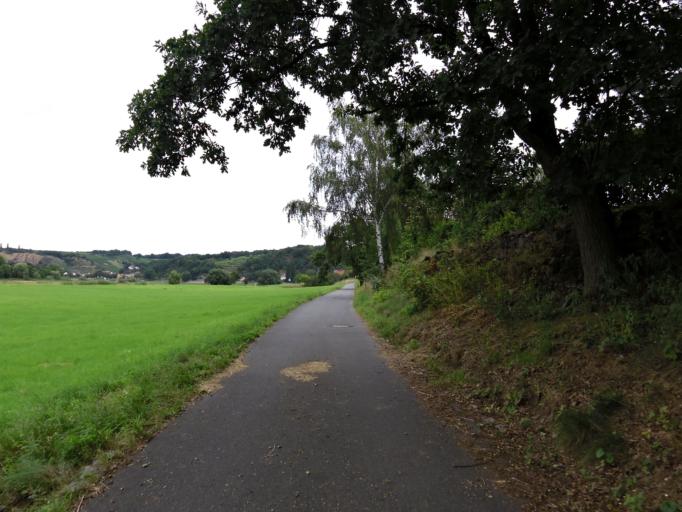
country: DE
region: Saxony
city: Weissig
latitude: 51.2237
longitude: 13.4176
